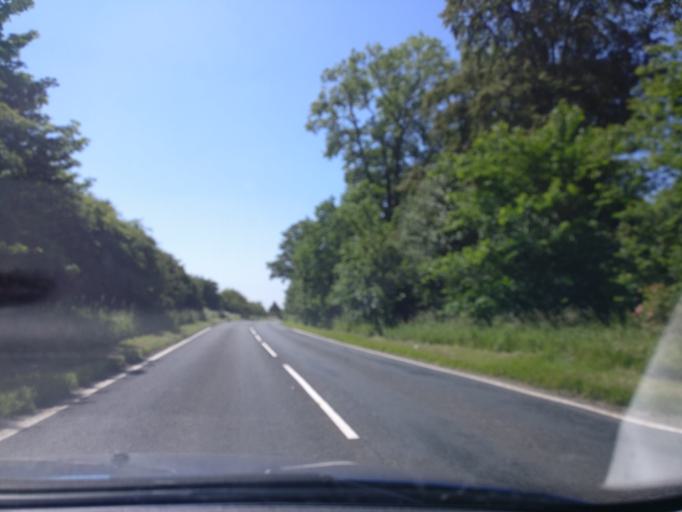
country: GB
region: Scotland
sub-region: East Lothian
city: Longniddry
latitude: 55.9804
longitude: -2.8774
